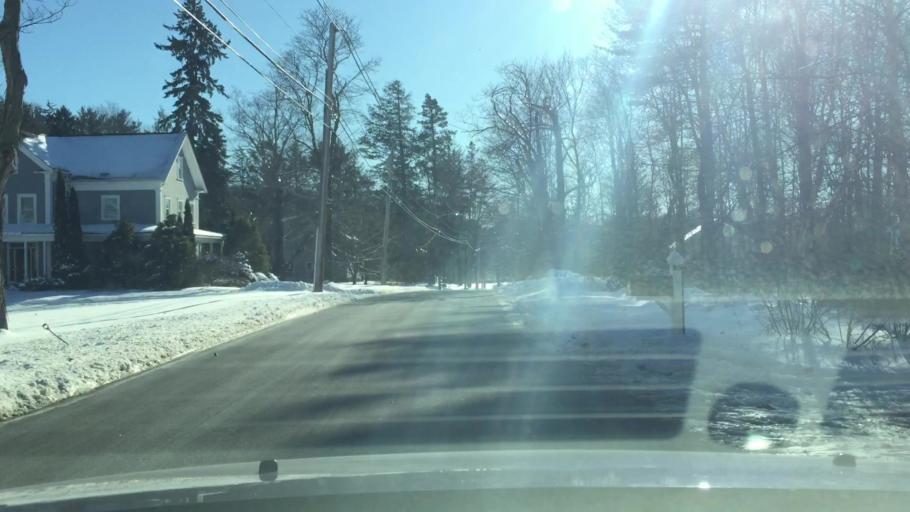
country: US
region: Massachusetts
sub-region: Essex County
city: North Andover
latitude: 42.6839
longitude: -71.0991
